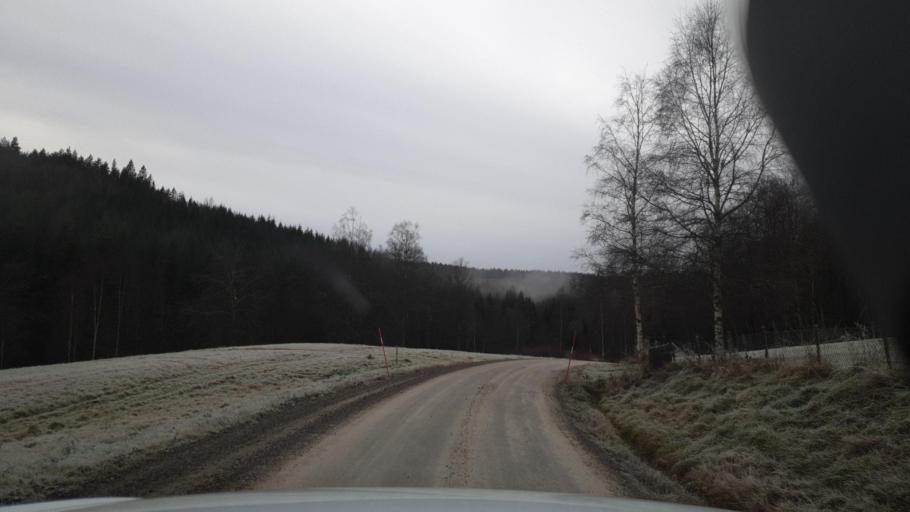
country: SE
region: Vaermland
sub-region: Arvika Kommun
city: Arvika
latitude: 59.7078
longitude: 12.8665
